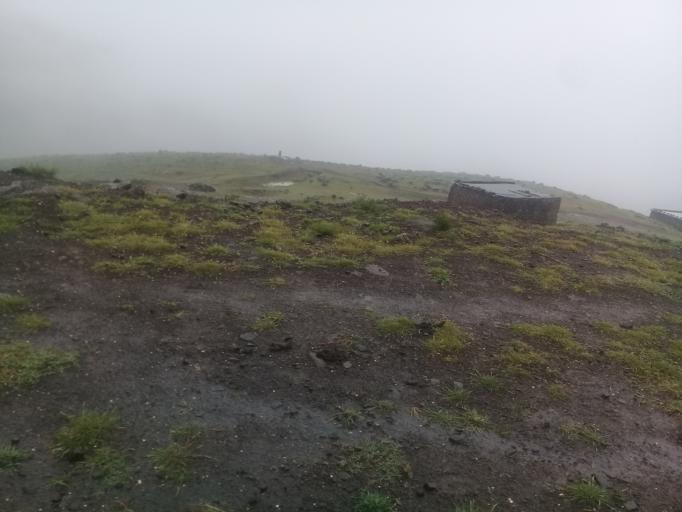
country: LS
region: Mokhotlong
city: Mokhotlong
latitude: -29.3778
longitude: 28.9849
